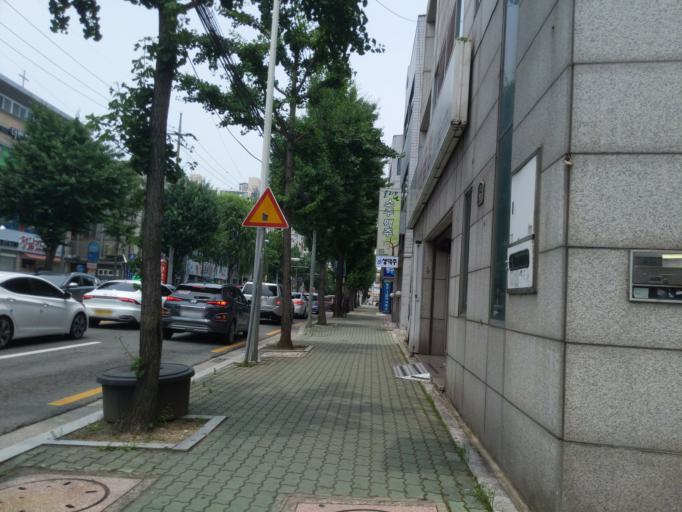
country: KR
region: Daegu
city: Hwawon
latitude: 35.8097
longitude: 128.5267
